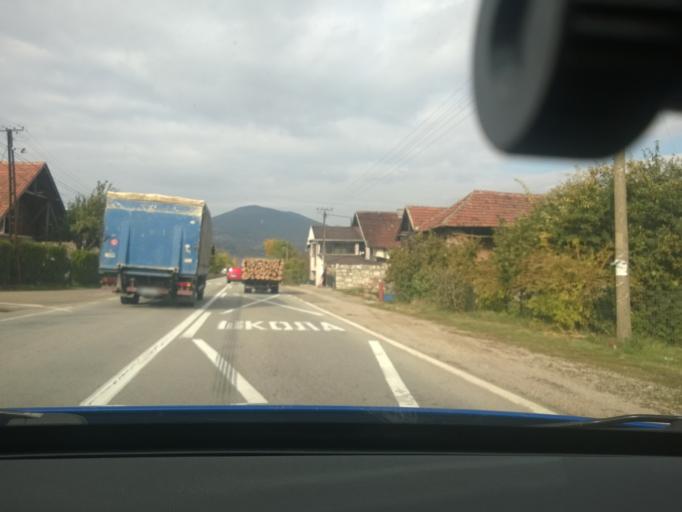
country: RS
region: Central Serbia
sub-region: Pirotski Okrug
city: Bela Palanka
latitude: 43.2944
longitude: 22.2085
